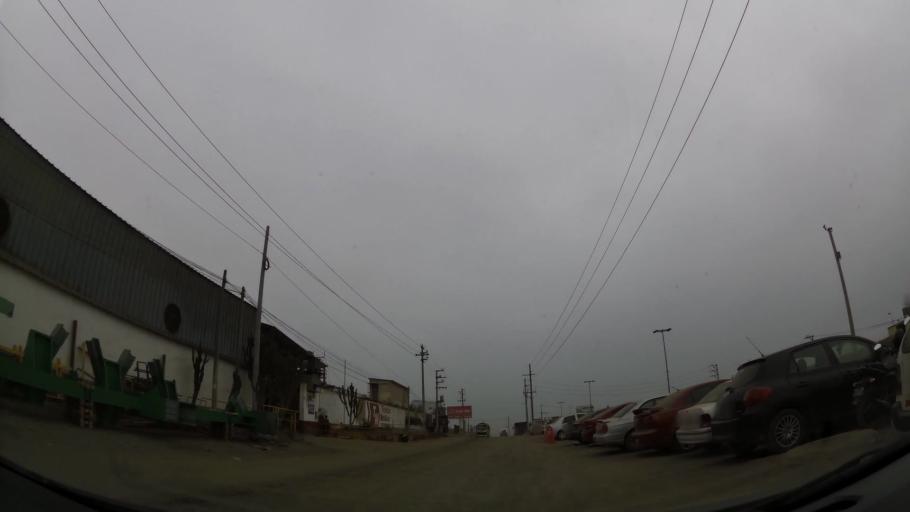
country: PE
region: Lima
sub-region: Lima
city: Surco
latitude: -12.2112
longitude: -76.9755
